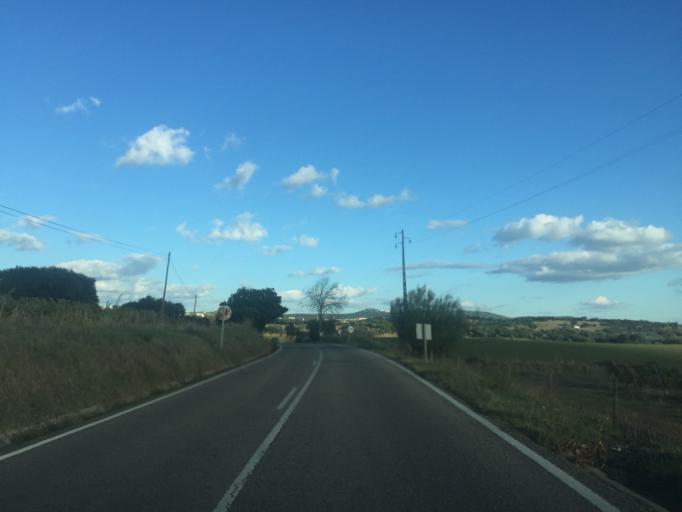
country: PT
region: Portalegre
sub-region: Alter do Chao
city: Alter do Chao
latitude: 39.1956
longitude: -7.6888
